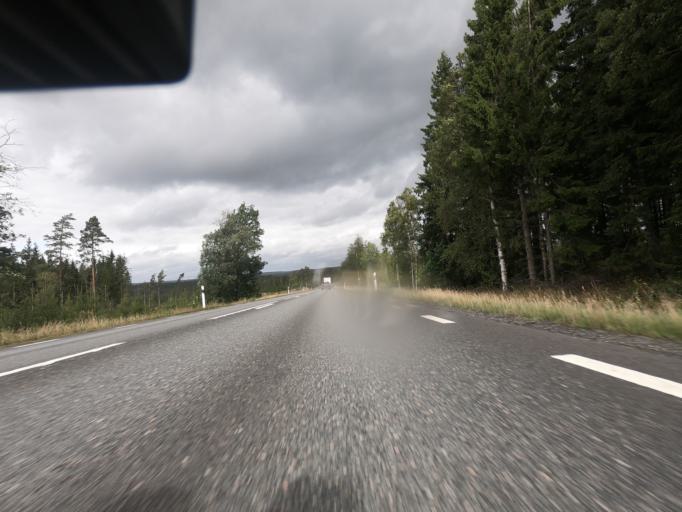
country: SE
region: Joenkoeping
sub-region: Savsjo Kommun
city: Vrigstad
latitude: 57.4220
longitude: 14.3298
